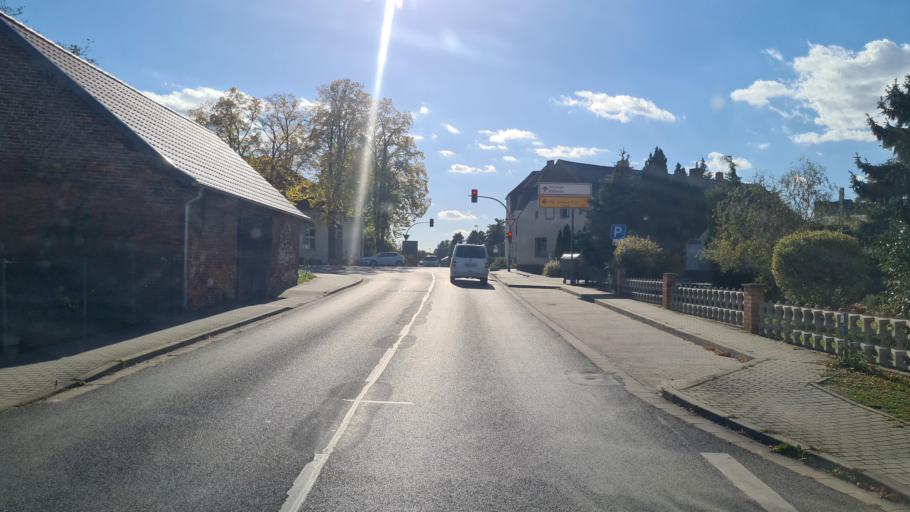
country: DE
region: Brandenburg
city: Kolkwitz
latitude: 51.7503
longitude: 14.2450
